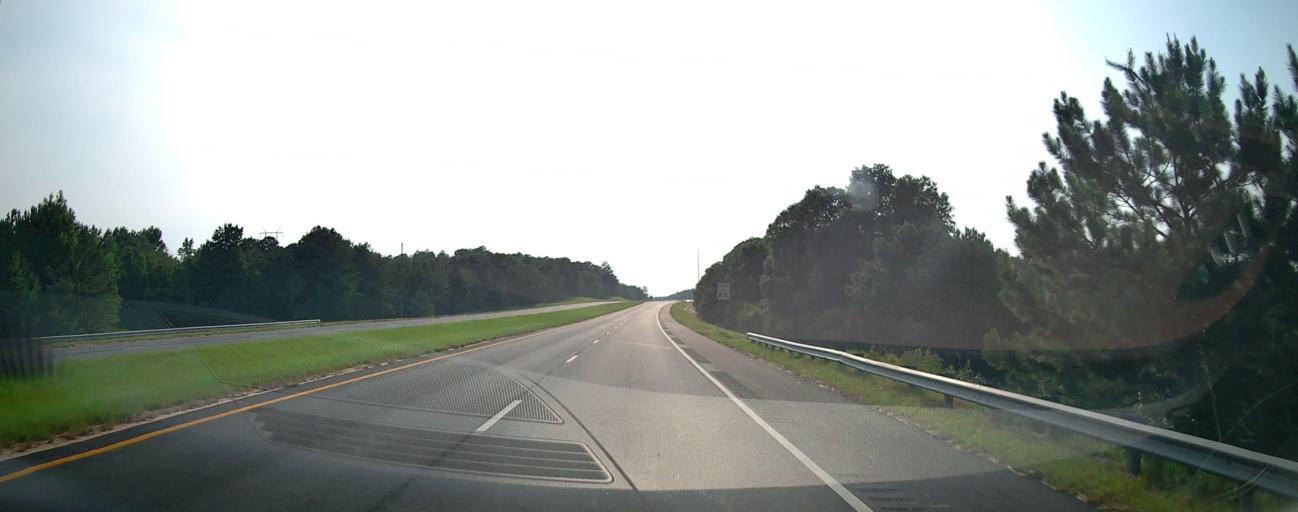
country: US
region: Georgia
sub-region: Taylor County
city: Butler
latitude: 32.5930
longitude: -84.3964
